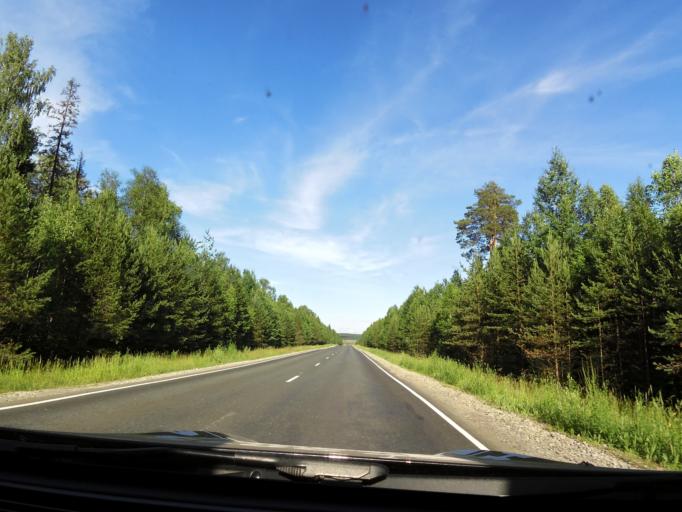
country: RU
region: Kirov
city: Chernaya Kholunitsa
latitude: 58.8589
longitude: 51.6628
